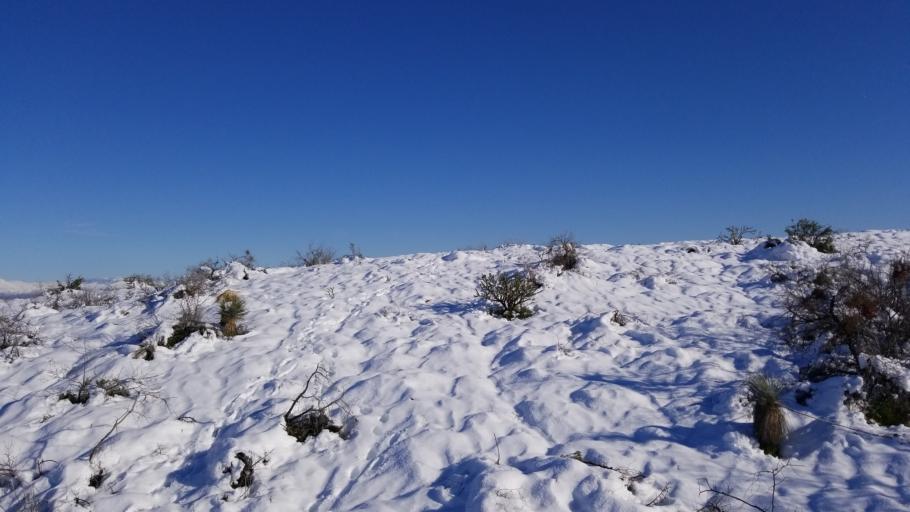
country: US
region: Arizona
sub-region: Maricopa County
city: Carefree
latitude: 33.8672
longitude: -111.8262
